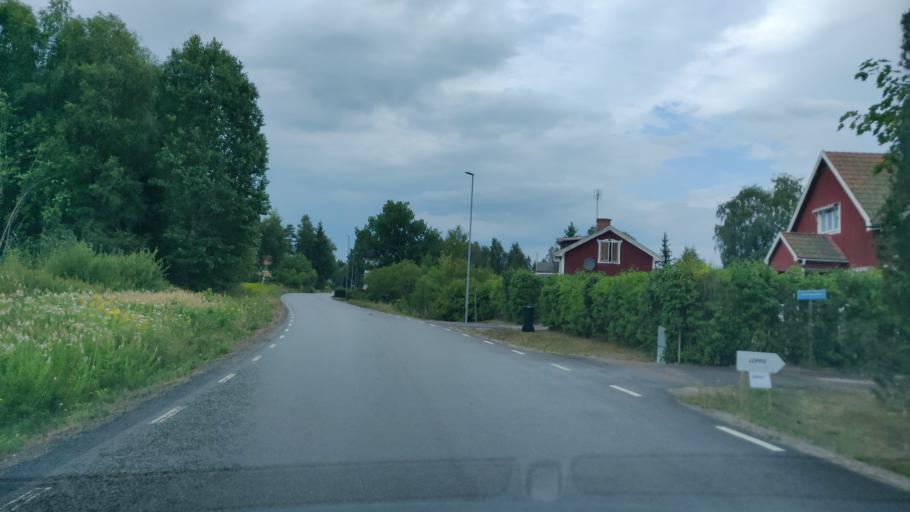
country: SE
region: Vaermland
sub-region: Munkfors Kommun
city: Munkfors
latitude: 59.8547
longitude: 13.5541
